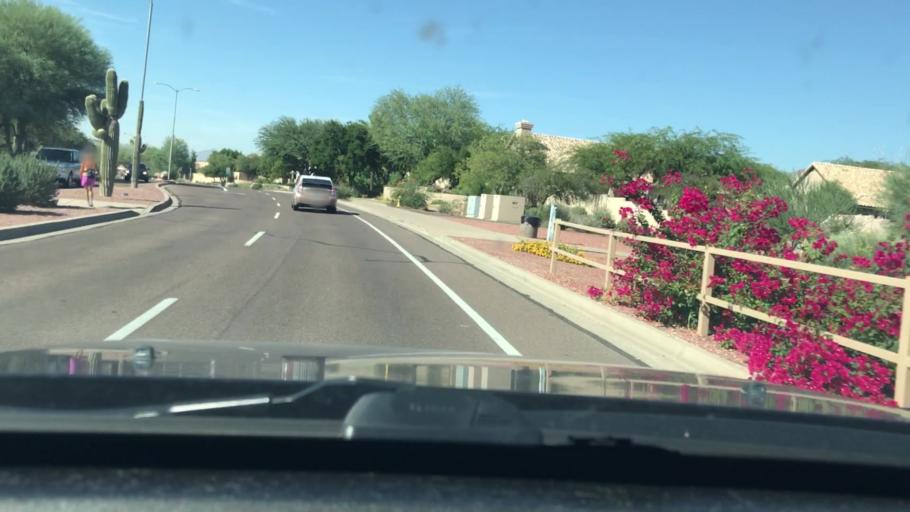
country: US
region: Arizona
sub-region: Maricopa County
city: Guadalupe
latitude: 33.3128
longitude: -112.0227
